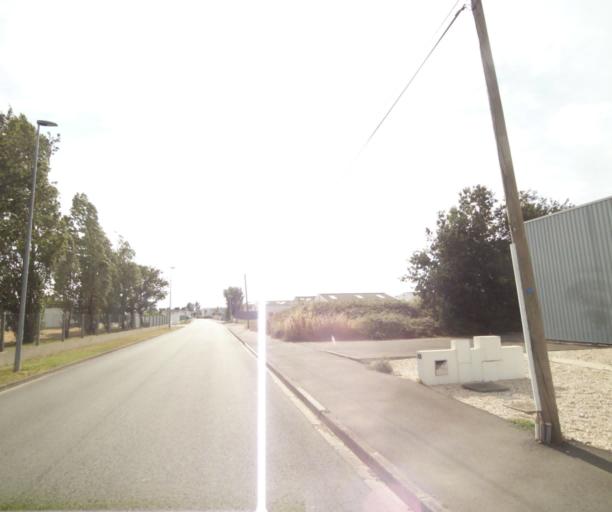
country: FR
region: Pays de la Loire
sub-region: Departement de la Vendee
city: Chateau-d'Olonne
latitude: 46.4884
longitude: -1.7295
